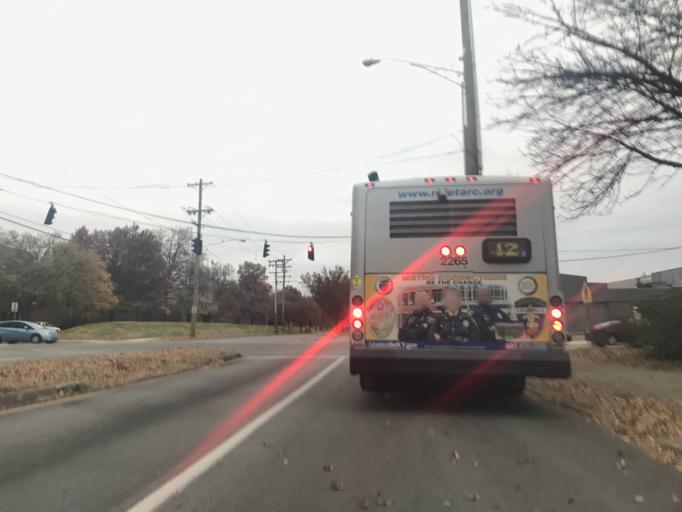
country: US
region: Kentucky
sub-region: Jefferson County
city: Louisville
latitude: 38.2531
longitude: -85.7725
